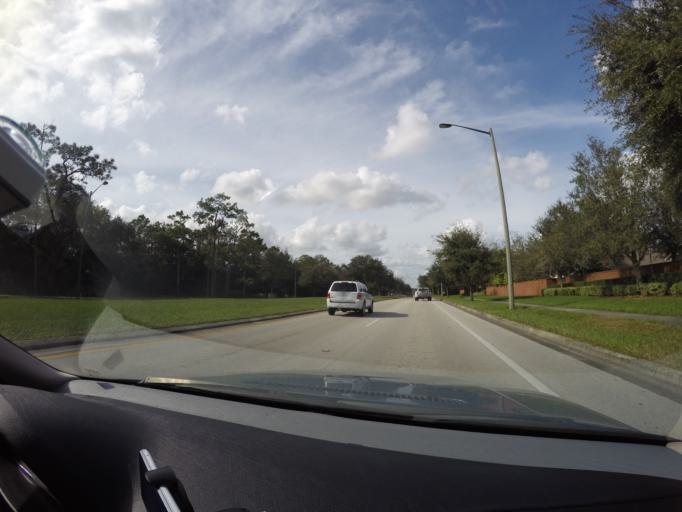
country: US
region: Florida
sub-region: Orange County
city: Conway
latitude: 28.4212
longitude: -81.2464
